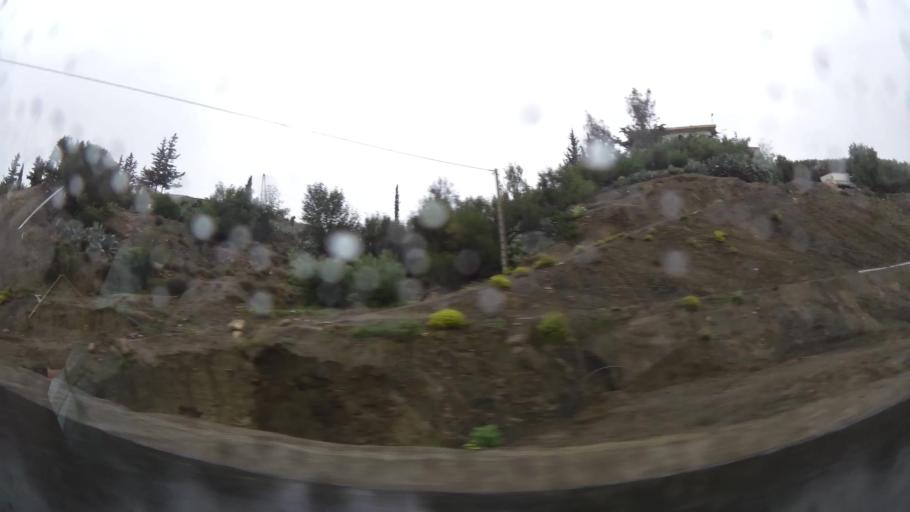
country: MA
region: Taza-Al Hoceima-Taounate
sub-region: Taza
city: Aknoul
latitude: 34.7919
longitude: -3.7528
